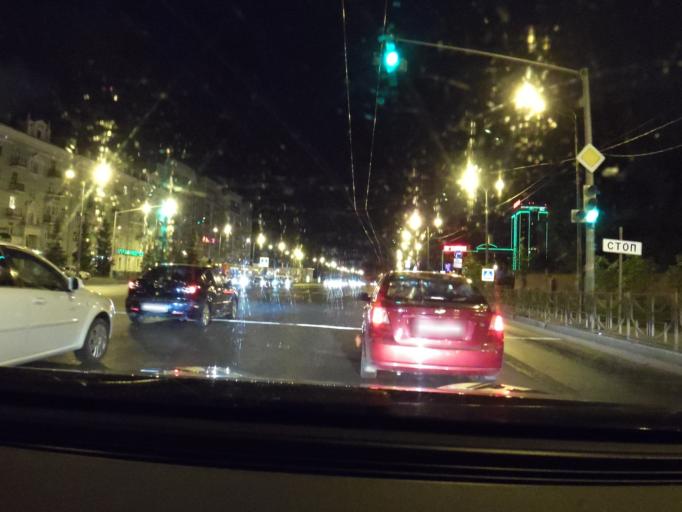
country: RU
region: Tatarstan
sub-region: Gorod Kazan'
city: Kazan
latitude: 55.7924
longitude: 49.1569
